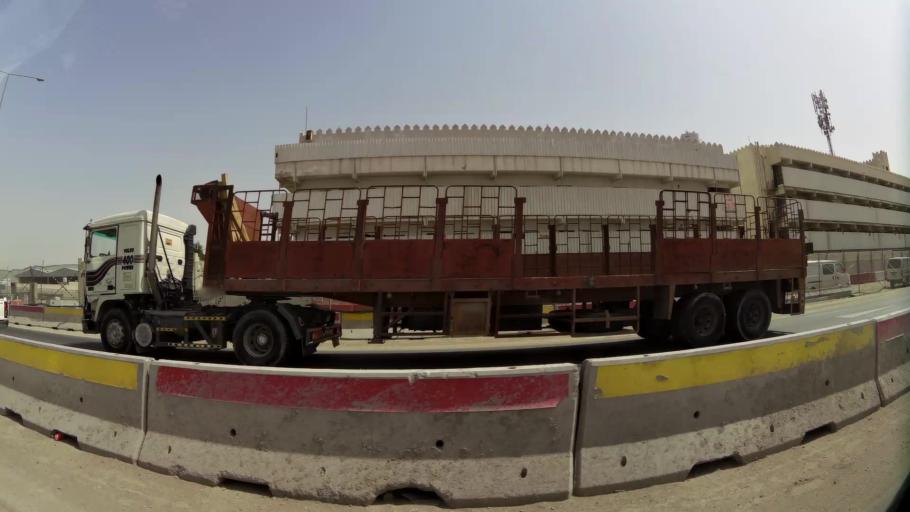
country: QA
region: Baladiyat ar Rayyan
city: Ar Rayyan
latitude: 25.1872
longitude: 51.4222
